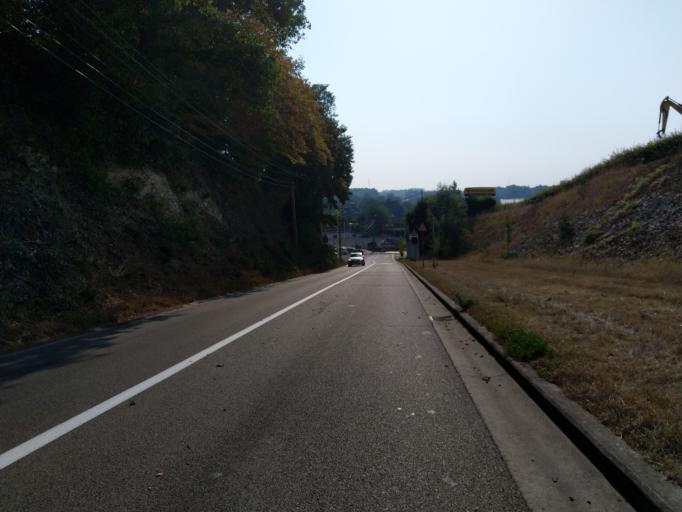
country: BE
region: Wallonia
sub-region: Province du Brabant Wallon
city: Ittre
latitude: 50.6087
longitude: 4.2173
